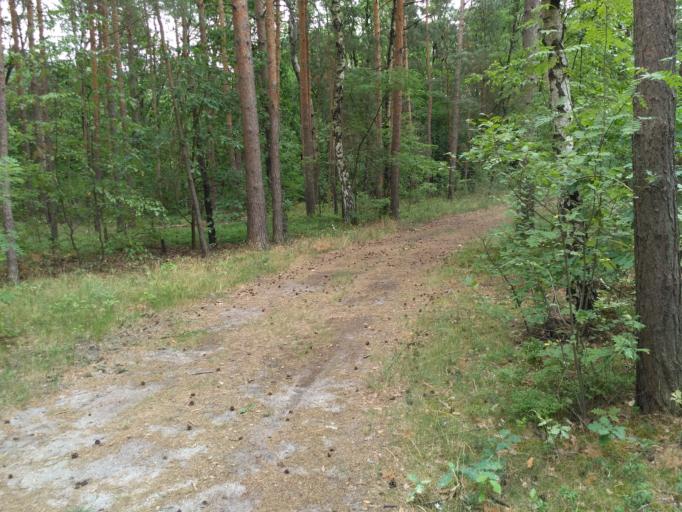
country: DE
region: Saxony
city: Hoyerswerda
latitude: 51.4547
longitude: 14.2863
